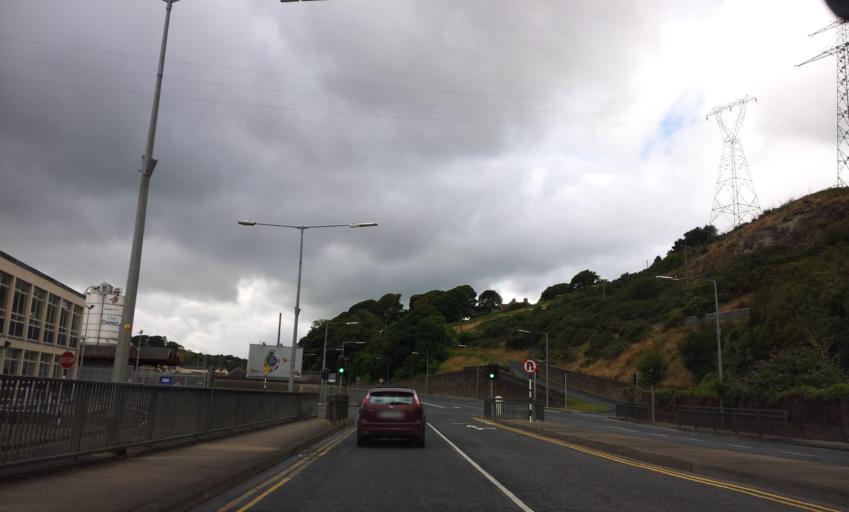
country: IE
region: Munster
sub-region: Waterford
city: Waterford
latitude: 52.2677
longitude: -7.1229
